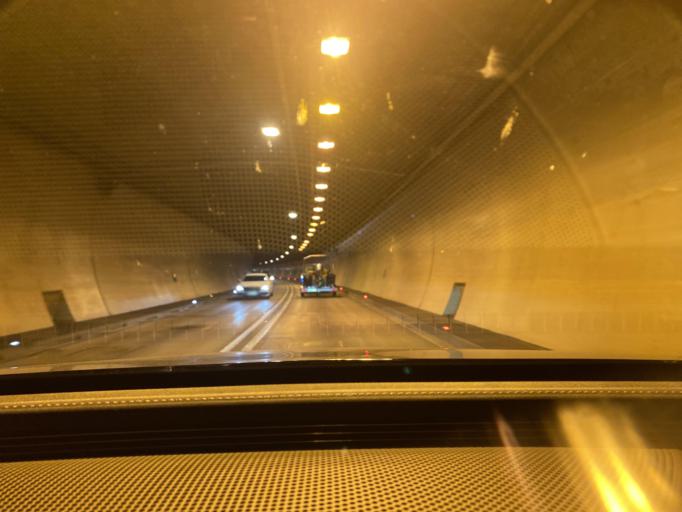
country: AT
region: Carinthia
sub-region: Politischer Bezirk Villach Land
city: Sankt Jakob
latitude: 46.5190
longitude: 14.0227
